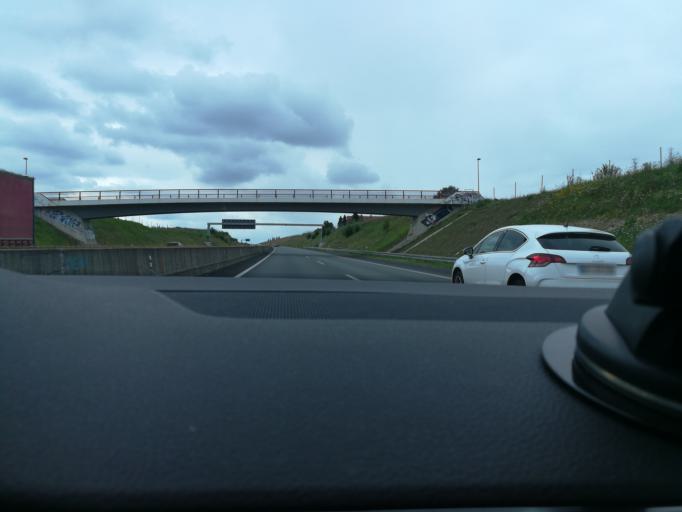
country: DE
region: North Rhine-Westphalia
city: Bad Oeynhausen
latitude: 52.2309
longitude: 8.7846
